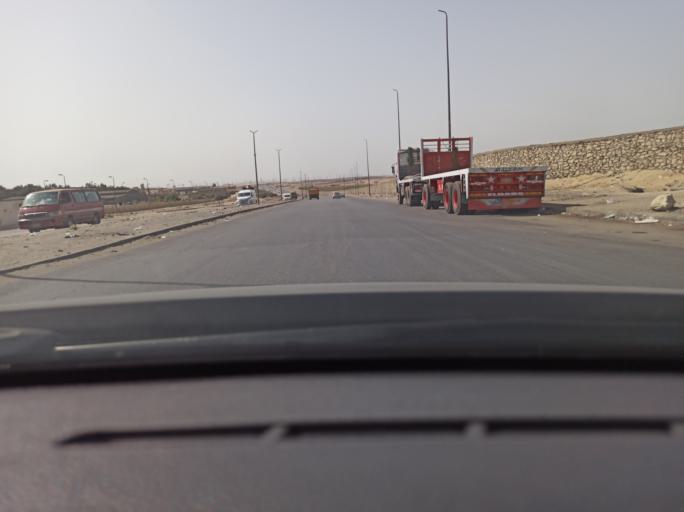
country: EG
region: Muhafazat al Qahirah
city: Halwan
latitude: 29.8185
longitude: 31.3520
